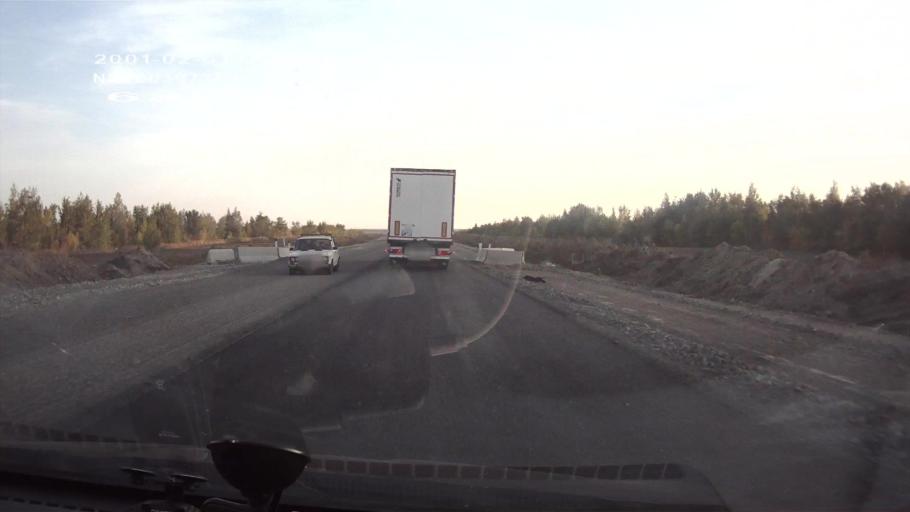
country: RU
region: Saratov
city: Krasnoarmeysk
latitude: 51.0032
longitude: 45.6150
